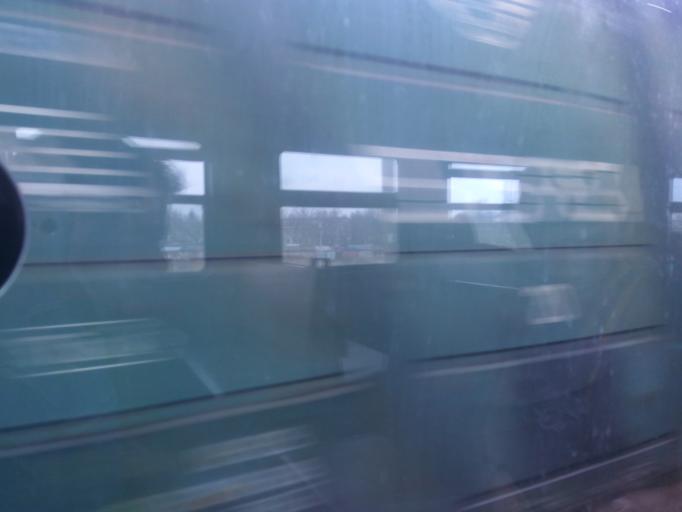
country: RU
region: Vladimir
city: Aleksandrov
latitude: 56.3905
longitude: 38.6854
